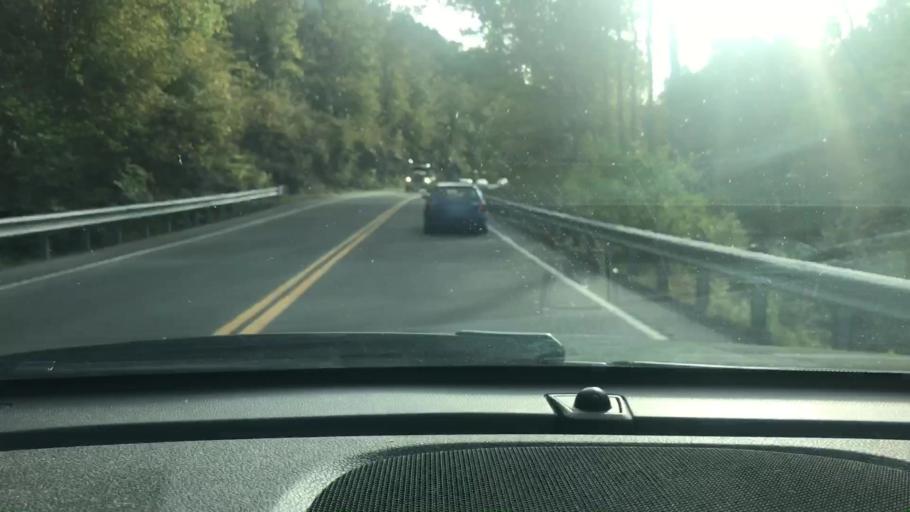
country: US
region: Tennessee
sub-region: Williamson County
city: Fairview
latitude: 36.0119
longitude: -87.0461
